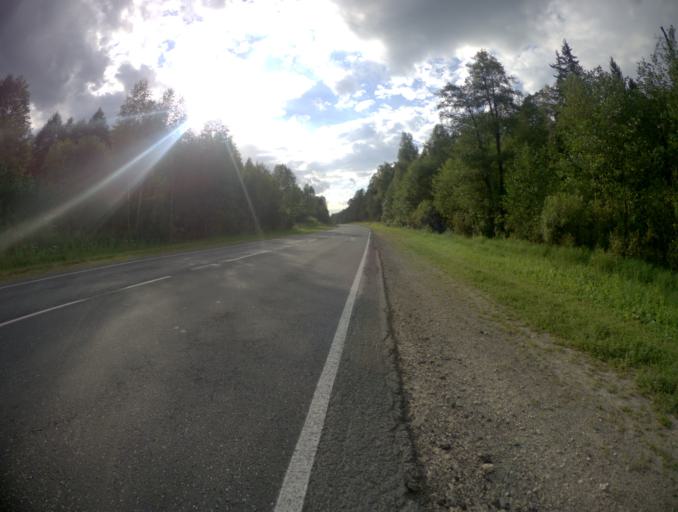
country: RU
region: Vladimir
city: Muromtsevo
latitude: 55.9545
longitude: 41.0014
